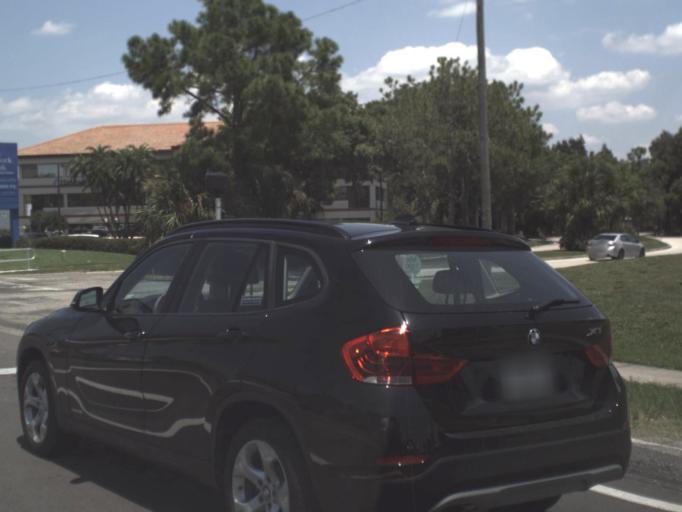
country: US
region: Florida
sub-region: Pinellas County
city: Saint George
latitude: 28.0273
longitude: -82.7380
